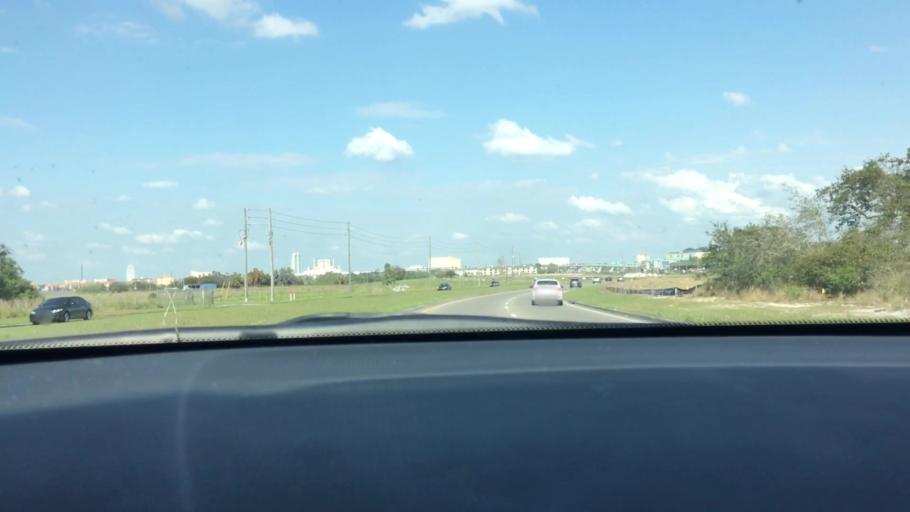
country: US
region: Florida
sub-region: Orange County
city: Williamsburg
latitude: 28.4002
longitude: -81.4871
